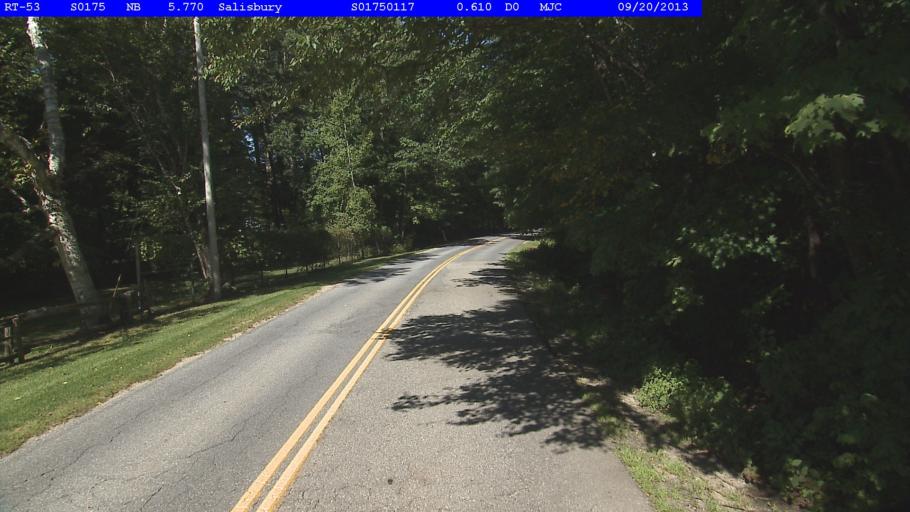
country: US
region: Vermont
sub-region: Rutland County
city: Brandon
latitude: 43.9063
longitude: -73.0663
